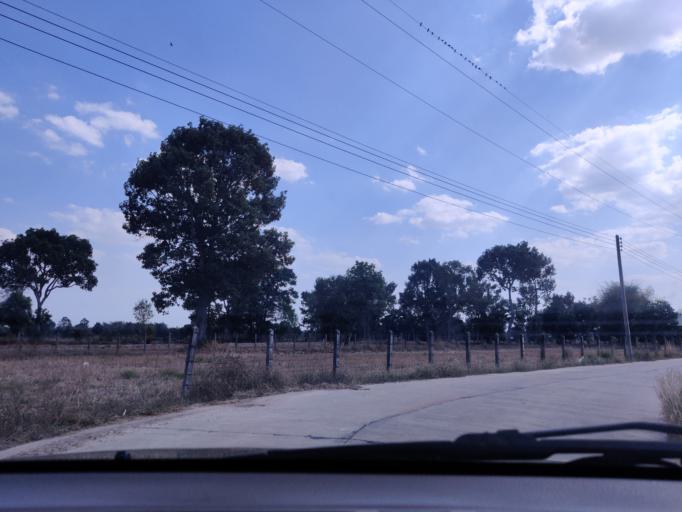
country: TH
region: Sisaket
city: Si Sa Ket
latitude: 15.0913
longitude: 104.3538
